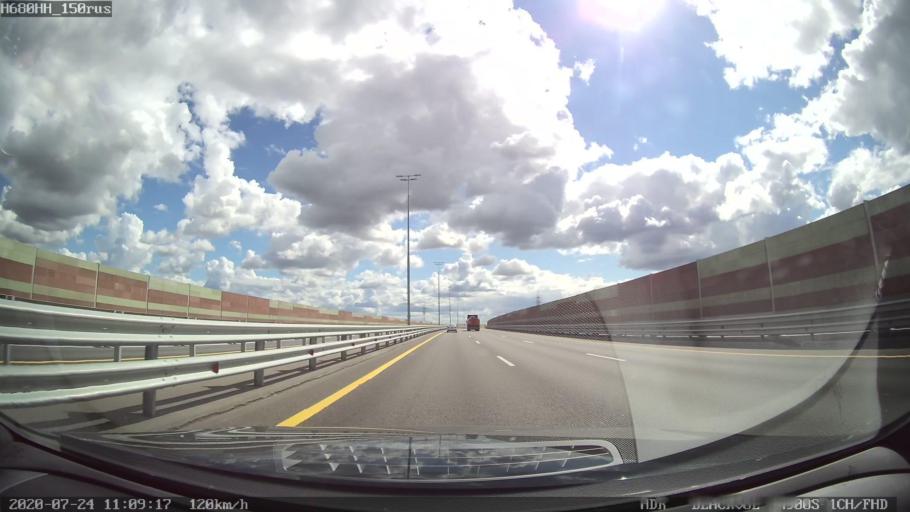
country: RU
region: St.-Petersburg
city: Tyarlevo
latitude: 59.7499
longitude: 30.4696
